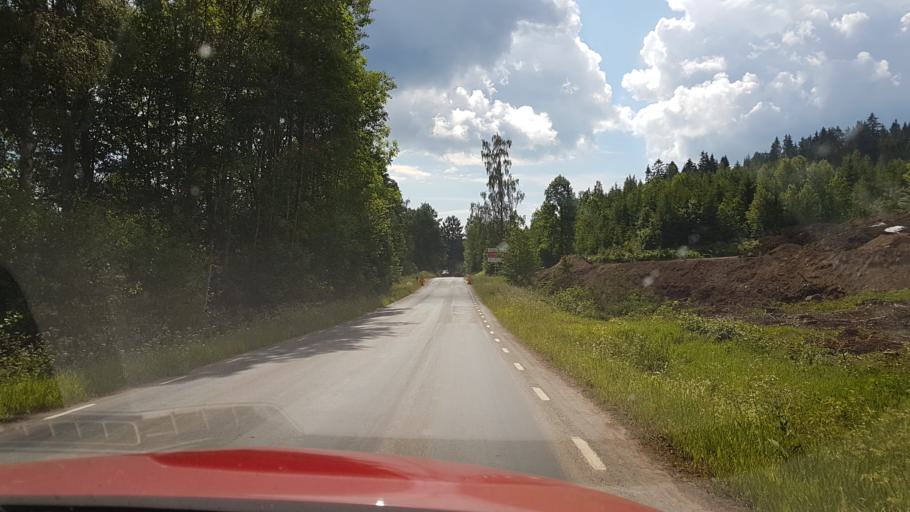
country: SE
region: Vaestra Goetaland
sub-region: Hjo Kommun
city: Hjo
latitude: 58.3089
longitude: 14.1914
